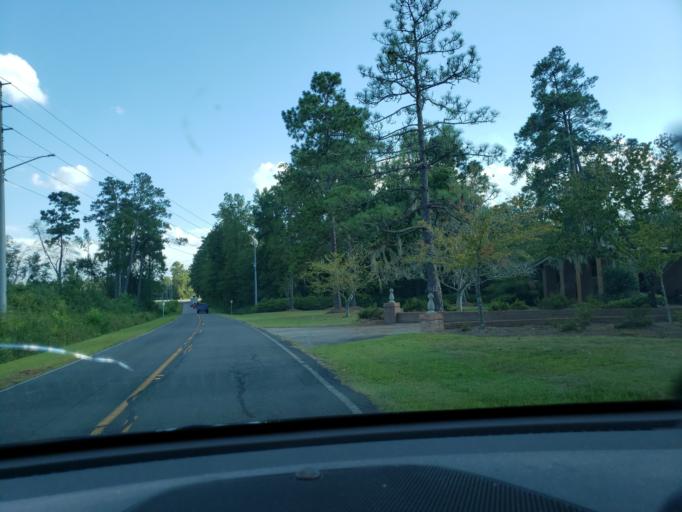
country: US
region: North Carolina
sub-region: Columbus County
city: Tabor City
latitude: 34.1625
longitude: -78.8518
